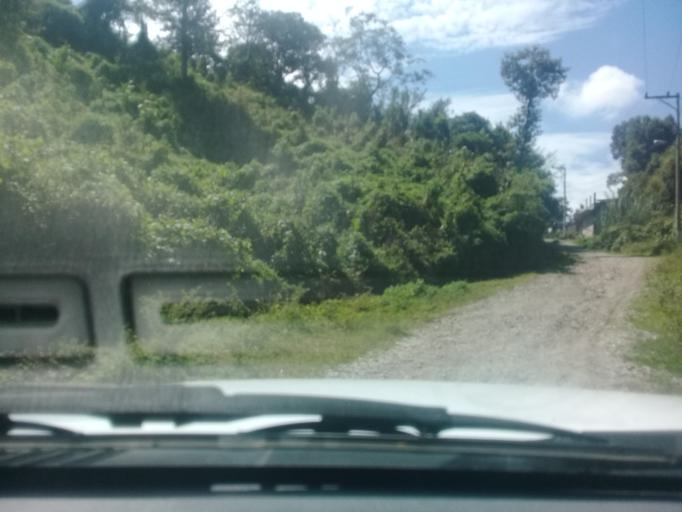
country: MX
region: Veracruz
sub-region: Tlalnelhuayocan
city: Otilpan
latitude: 19.5646
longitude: -96.9758
